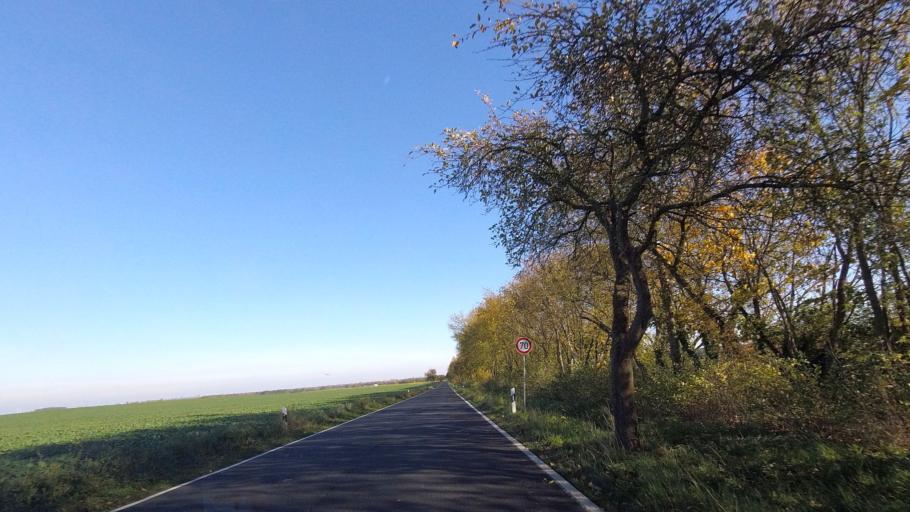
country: DE
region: Saxony-Anhalt
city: Zahna
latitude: 51.9730
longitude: 12.8420
